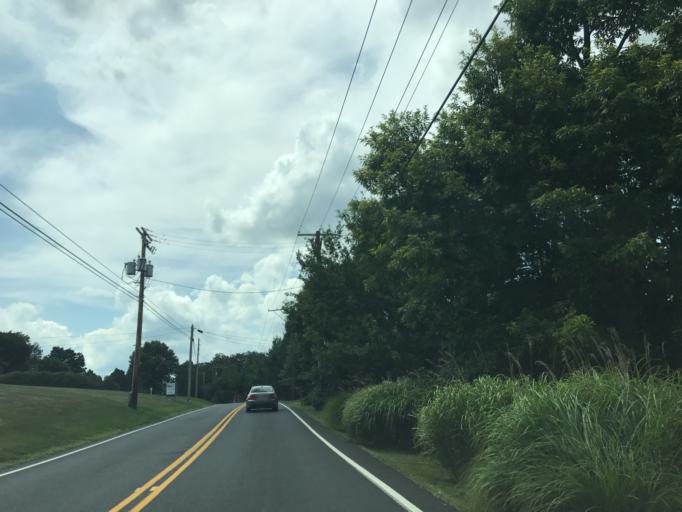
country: US
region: Pennsylvania
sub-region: Lancaster County
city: Penryn
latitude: 40.2076
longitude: -76.3834
